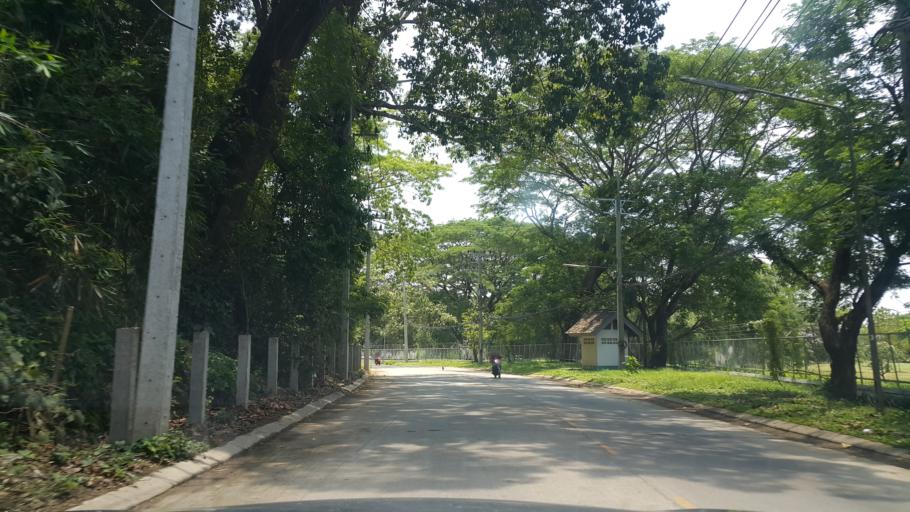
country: TH
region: Chiang Rai
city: Chiang Rai
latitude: 19.9155
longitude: 99.8221
